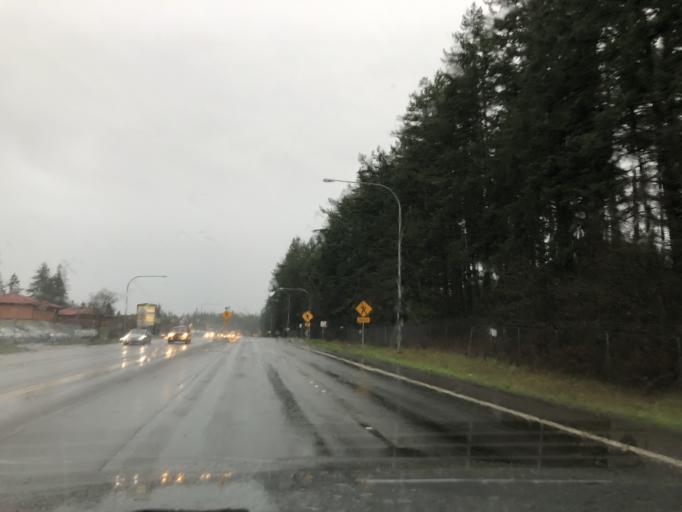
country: US
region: Washington
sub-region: Pierce County
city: Spanaway
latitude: 47.0908
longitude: -122.4351
